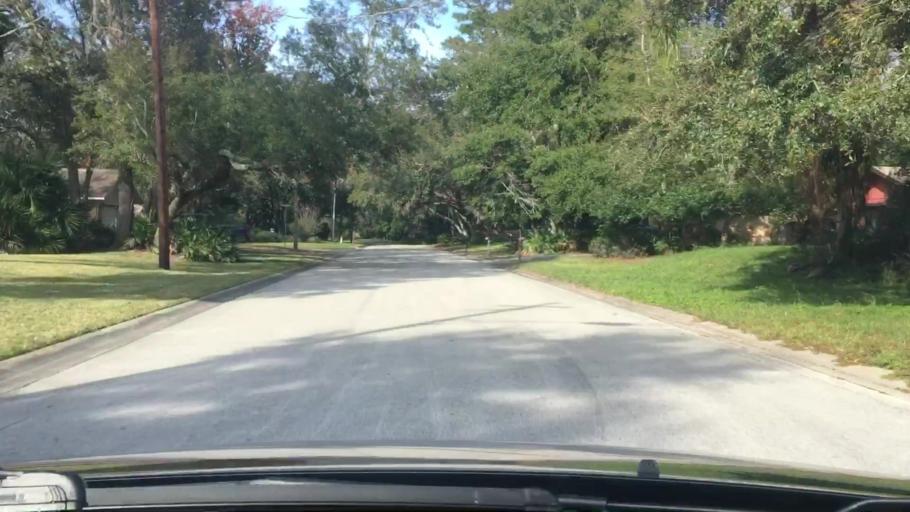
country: US
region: Florida
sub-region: Volusia County
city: Ormond Beach
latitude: 29.2735
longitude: -81.1010
